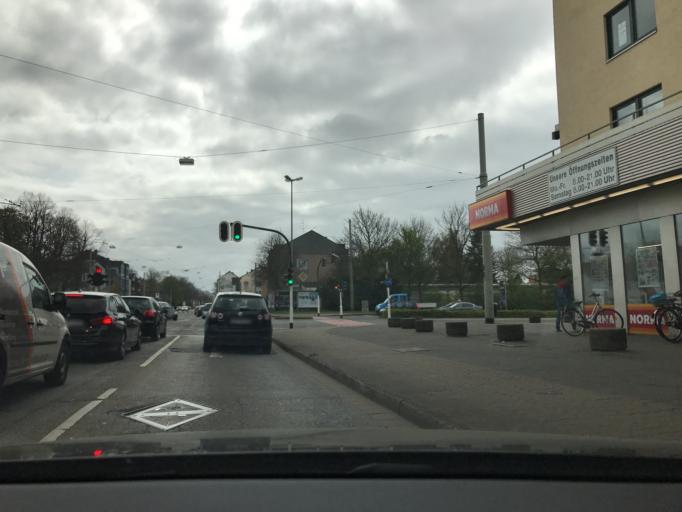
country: DE
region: North Rhine-Westphalia
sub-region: Regierungsbezirk Dusseldorf
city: Krefeld
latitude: 51.3170
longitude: 6.5756
